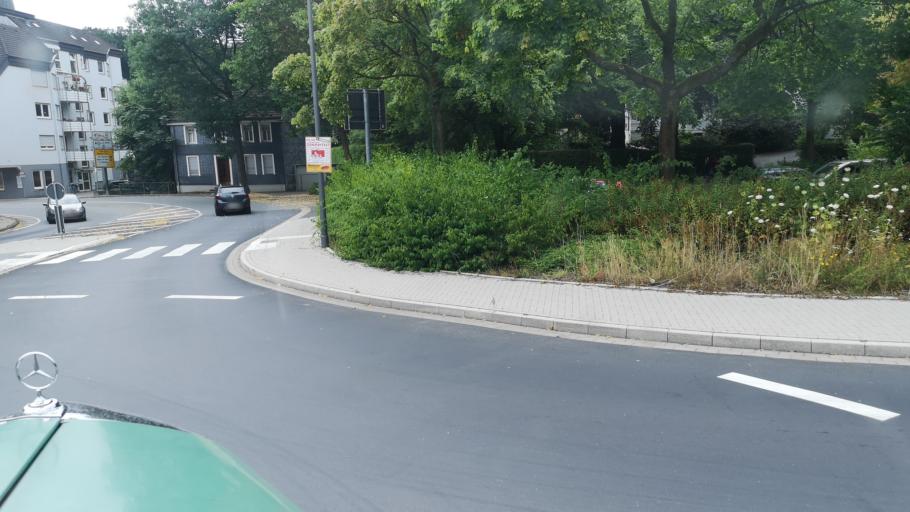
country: DE
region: North Rhine-Westphalia
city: Wipperfurth
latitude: 51.1166
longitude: 7.3899
